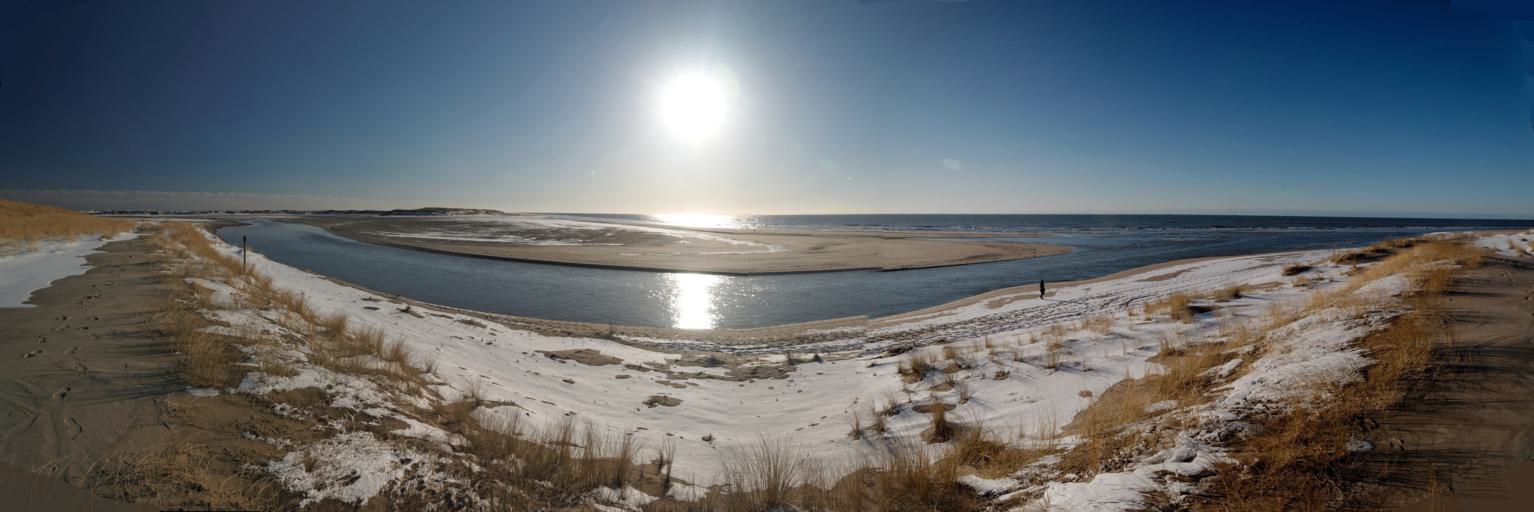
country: NL
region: North Holland
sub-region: Gemeente Texel
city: Den Burg
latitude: 53.1423
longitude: 4.8019
